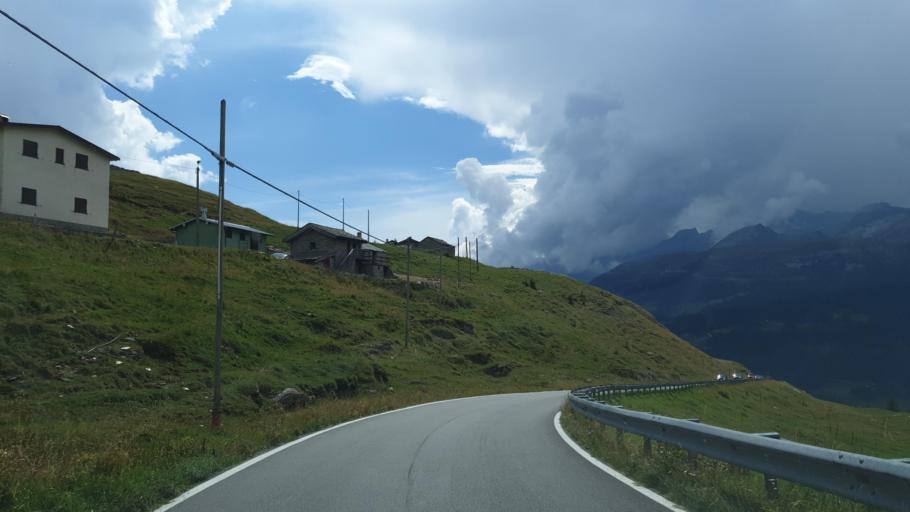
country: IT
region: Lombardy
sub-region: Provincia di Sondrio
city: Campodolcino
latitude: 46.4583
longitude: 9.3383
